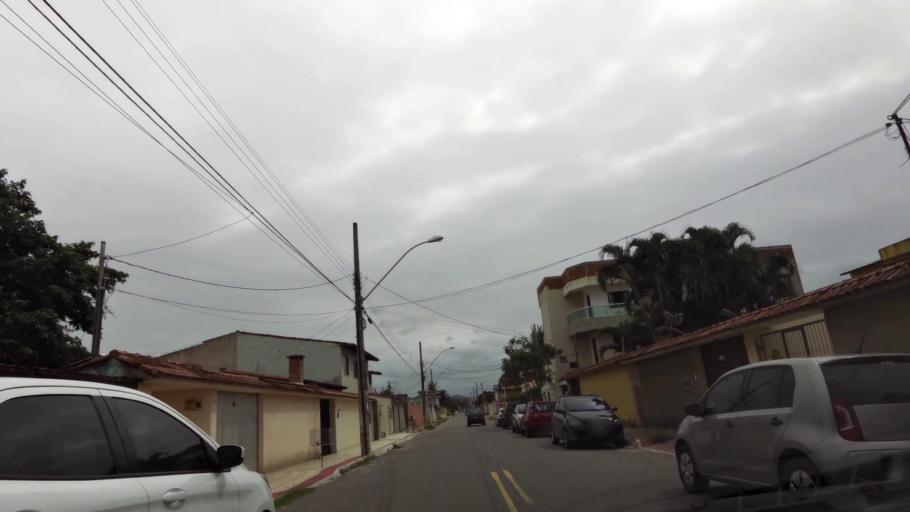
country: BR
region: Espirito Santo
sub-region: Guarapari
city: Guarapari
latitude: -20.6642
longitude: -40.5051
